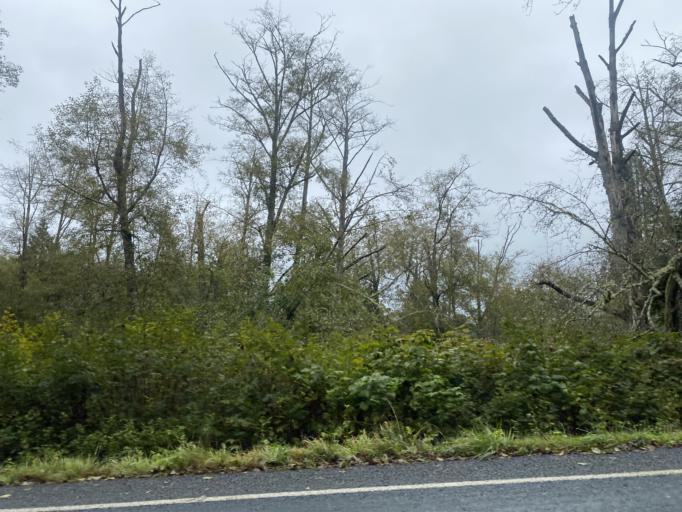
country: US
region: Washington
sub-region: Island County
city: Langley
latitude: 48.0471
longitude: -122.4373
